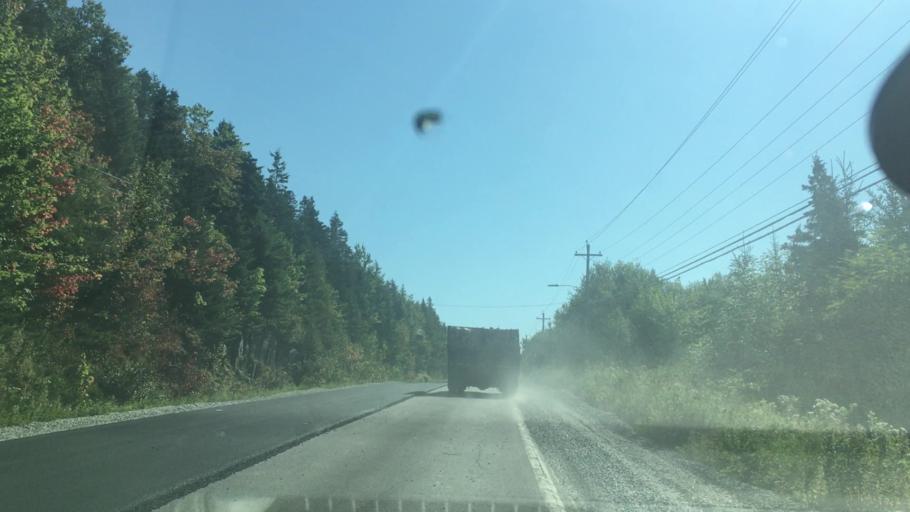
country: CA
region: Nova Scotia
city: New Glasgow
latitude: 44.9101
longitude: -62.5040
